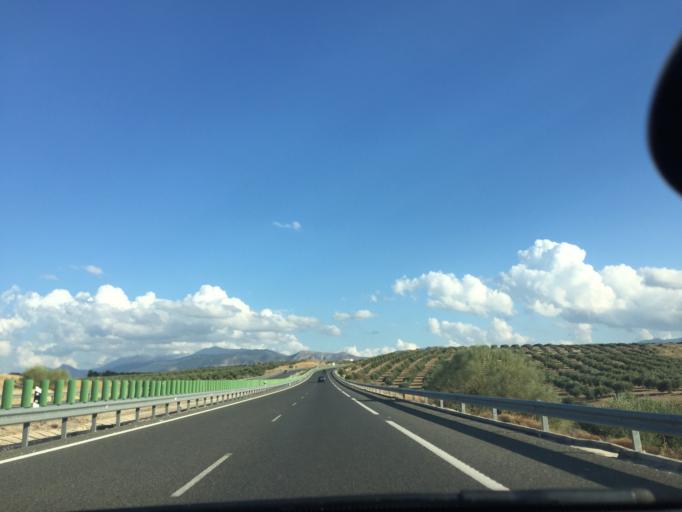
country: ES
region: Andalusia
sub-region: Provincia de Jaen
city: Jaen
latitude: 37.8189
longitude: -3.7417
